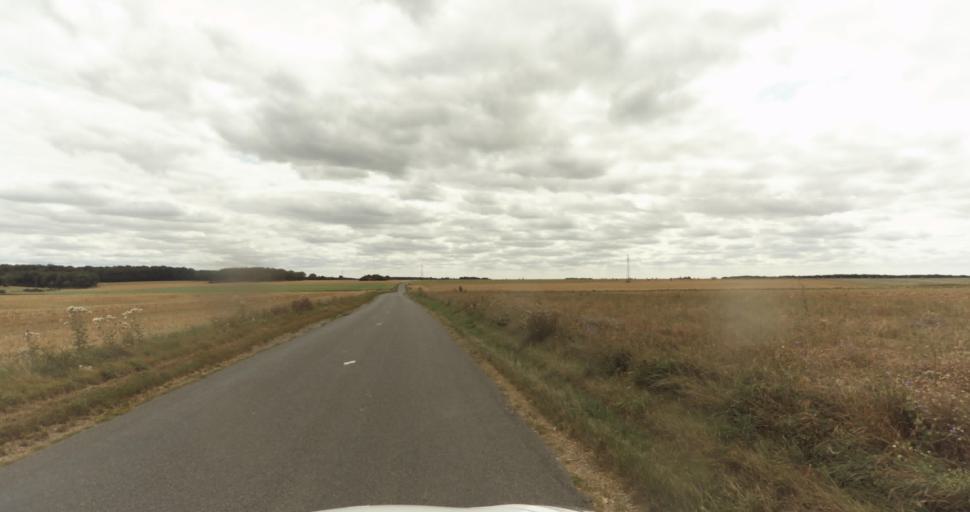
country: FR
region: Haute-Normandie
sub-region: Departement de l'Eure
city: Saint-Germain-sur-Avre
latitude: 48.7913
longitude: 1.2845
